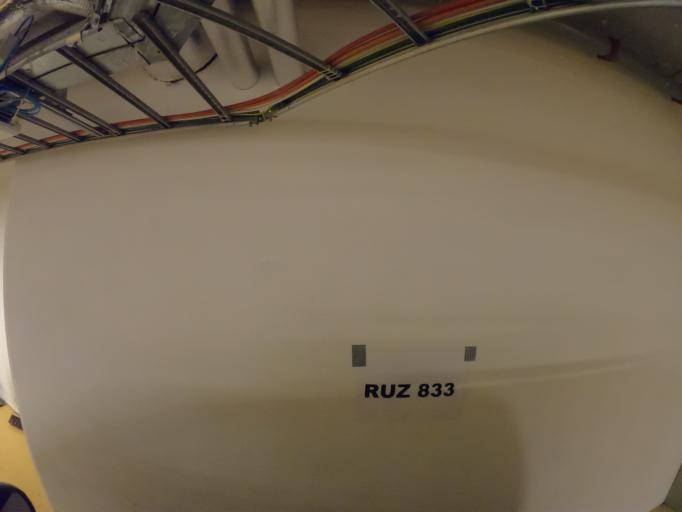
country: SE
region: Skane
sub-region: Osby Kommun
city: Lonsboda
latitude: 56.3992
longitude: 14.2018
